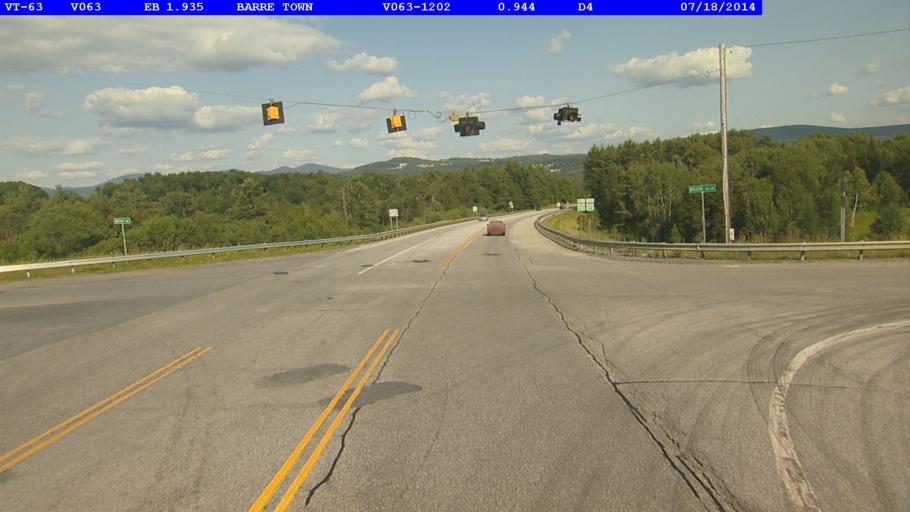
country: US
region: Vermont
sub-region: Washington County
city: South Barre
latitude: 44.1653
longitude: -72.5402
